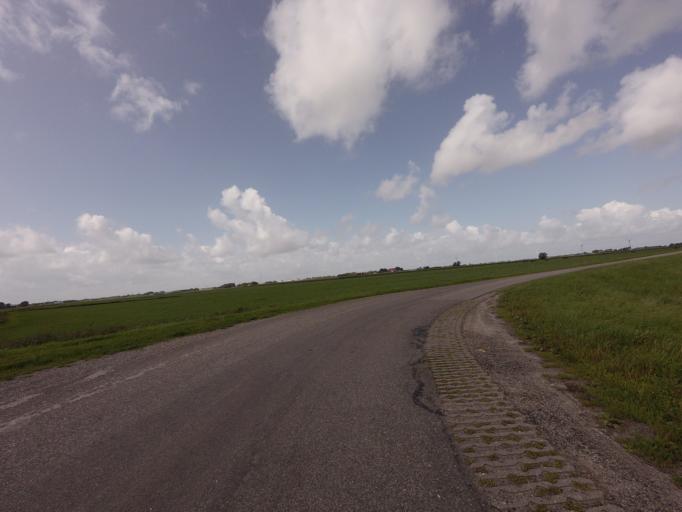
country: NL
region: Friesland
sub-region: Gemeente Franekeradeel
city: Sexbierum
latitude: 53.1680
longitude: 5.4858
